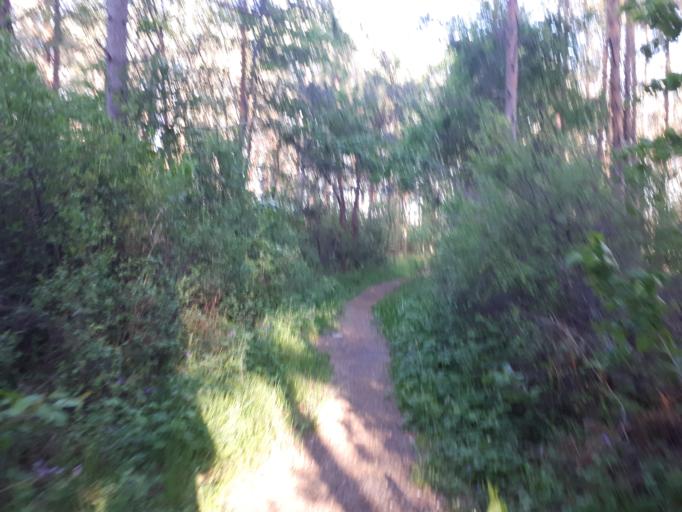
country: SE
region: Gotland
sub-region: Gotland
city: Visby
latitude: 57.6026
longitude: 18.3005
